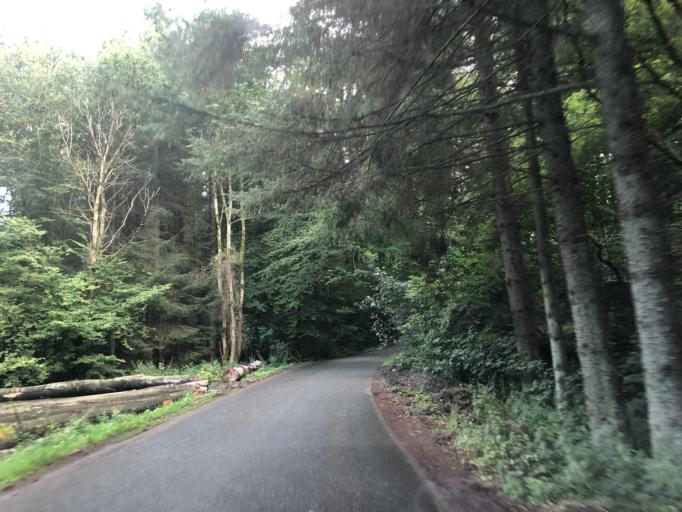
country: DK
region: South Denmark
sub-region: Vejle Kommune
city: Borkop
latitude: 55.6856
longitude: 9.6016
